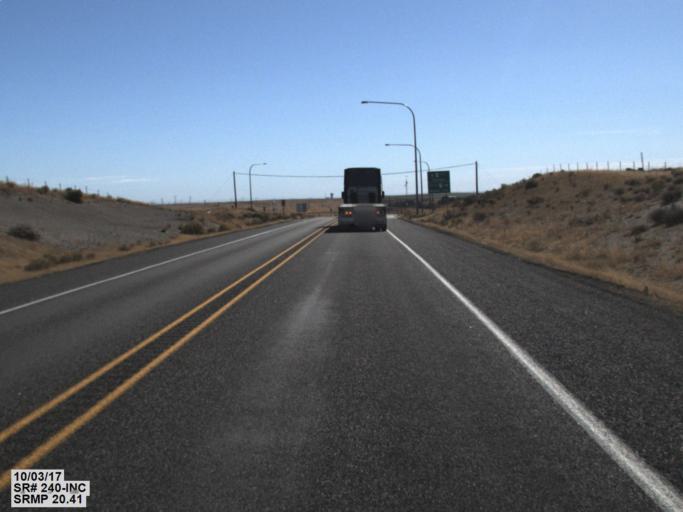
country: US
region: Washington
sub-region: Benton County
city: West Richland
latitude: 46.3839
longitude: -119.4240
